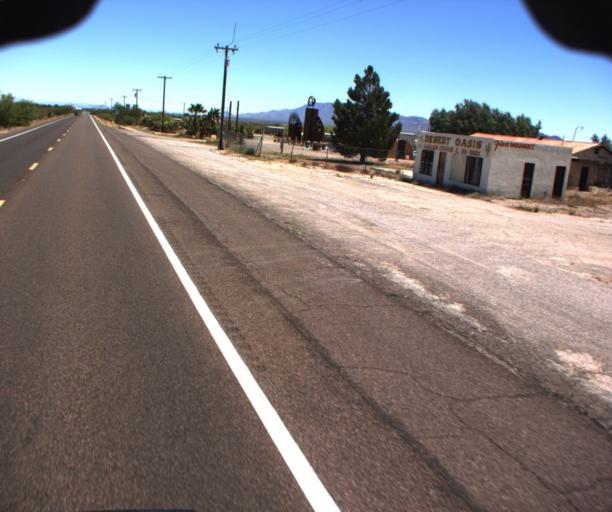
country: US
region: Arizona
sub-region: La Paz County
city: Salome
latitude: 33.7696
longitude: -113.6365
